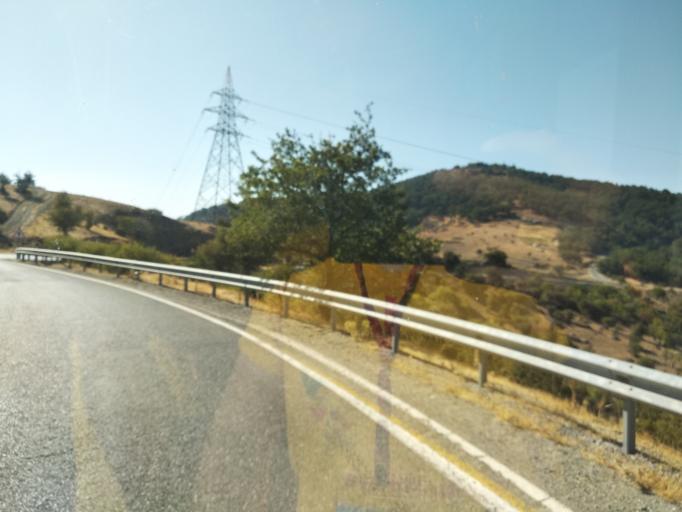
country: TR
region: Izmir
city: Gaziemir
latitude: 38.3256
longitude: 27.0053
